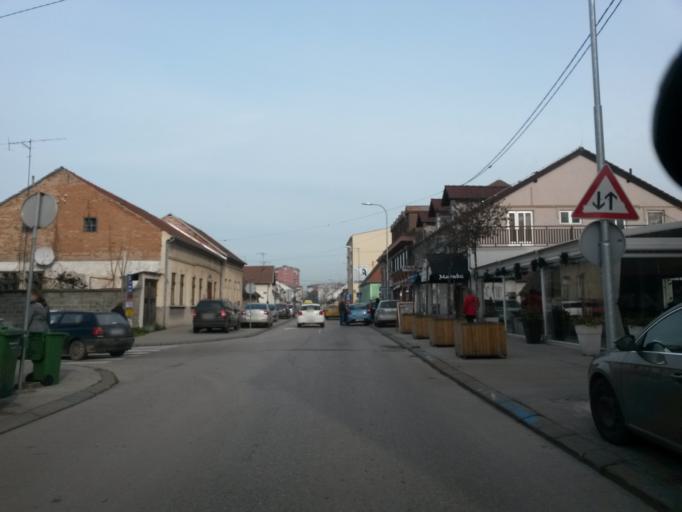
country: HR
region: Vukovarsko-Srijemska
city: Vinkovci
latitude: 45.2888
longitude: 18.8021
